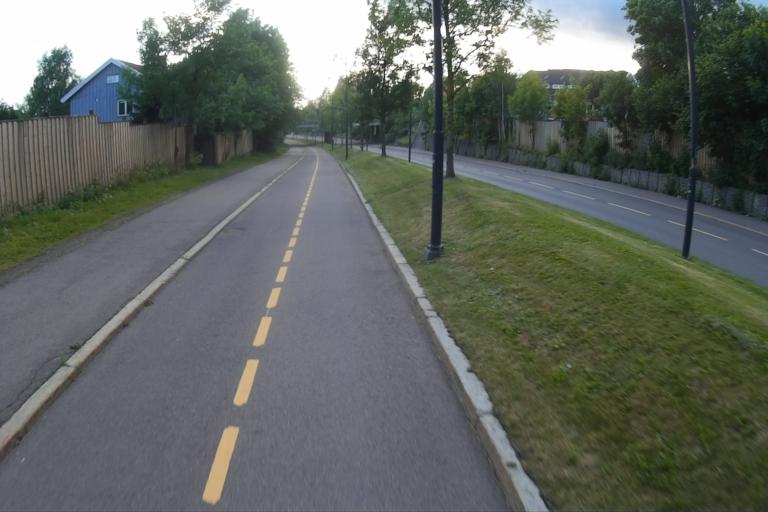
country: NO
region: Oslo
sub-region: Oslo
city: Oslo
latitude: 59.9530
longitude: 10.7550
